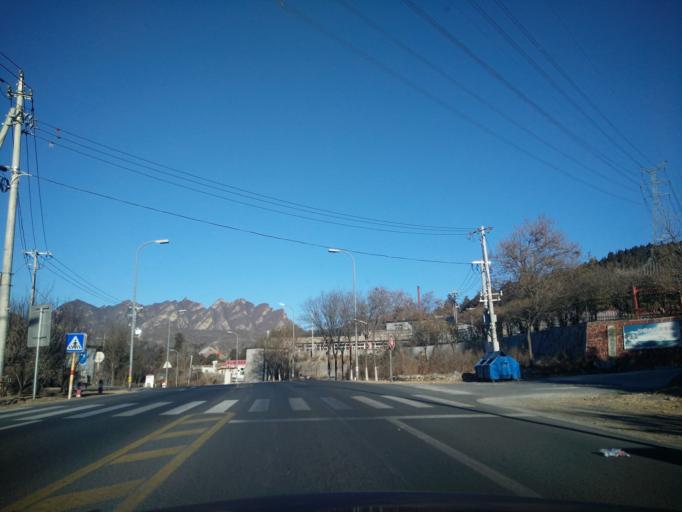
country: CN
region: Beijing
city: Miaofengshan
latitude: 39.9795
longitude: 116.0383
